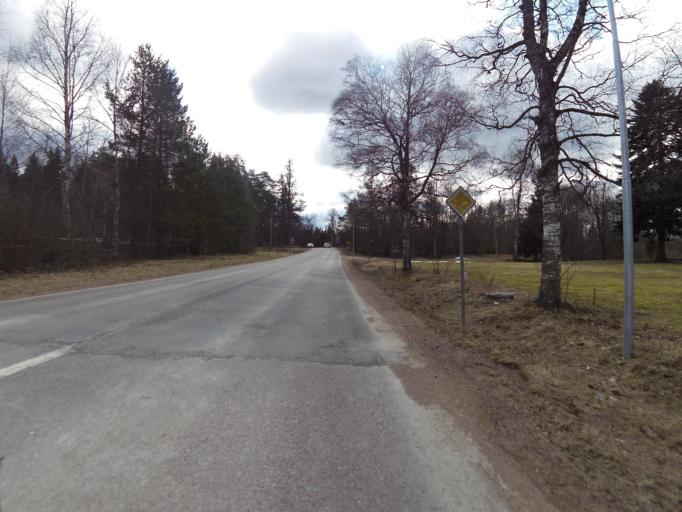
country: SE
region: Dalarna
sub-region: Avesta Kommun
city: Avesta
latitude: 60.3141
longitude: 16.2063
